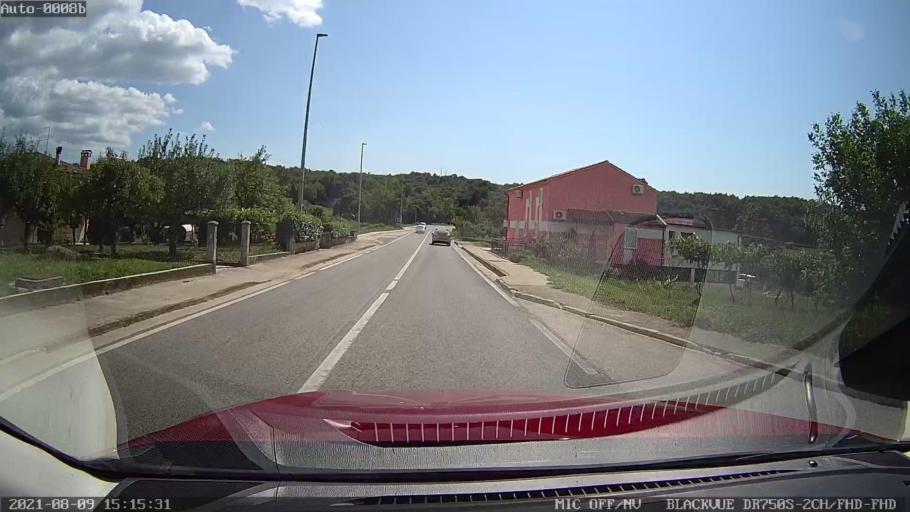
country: HR
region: Istarska
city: Pazin
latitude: 45.2355
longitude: 13.9235
